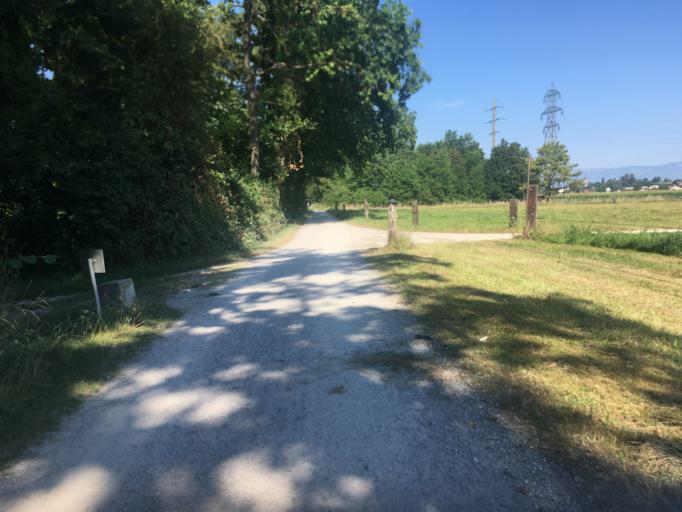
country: CH
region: Bern
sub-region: Emmental District
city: Lyssach
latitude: 47.0709
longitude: 7.6025
